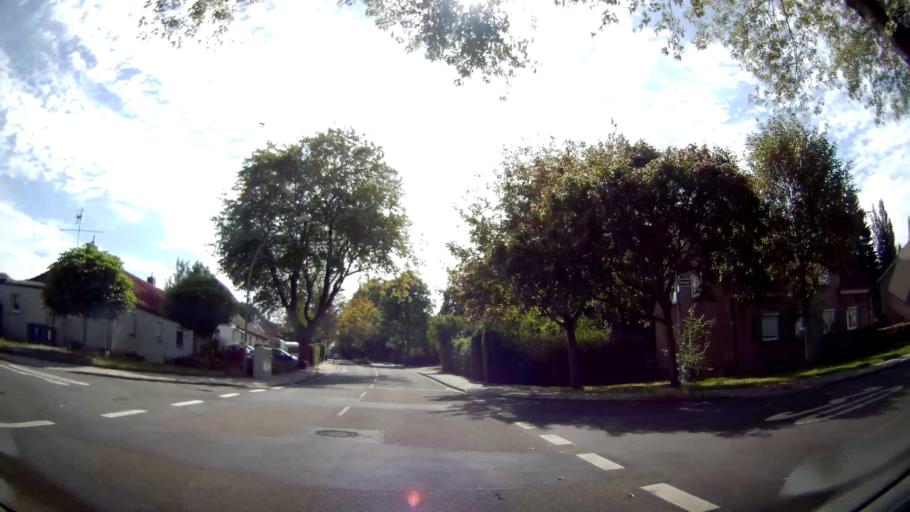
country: DE
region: North Rhine-Westphalia
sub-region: Regierungsbezirk Munster
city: Gladbeck
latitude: 51.5494
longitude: 7.0265
